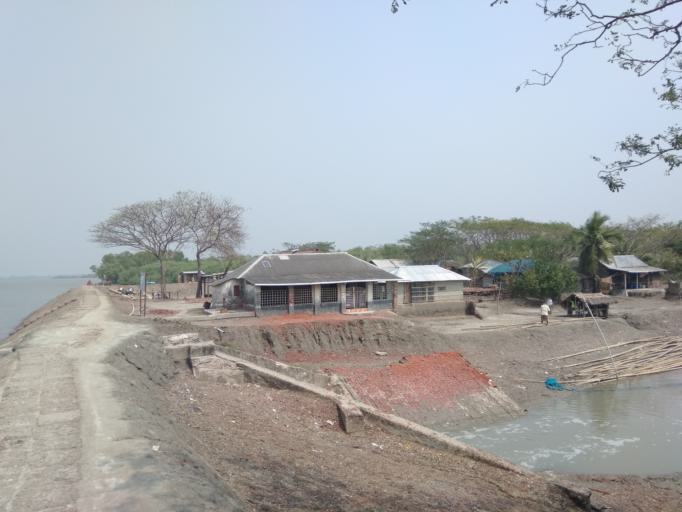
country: IN
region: West Bengal
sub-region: North 24 Parganas
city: Gosaba
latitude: 22.2549
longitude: 89.2506
